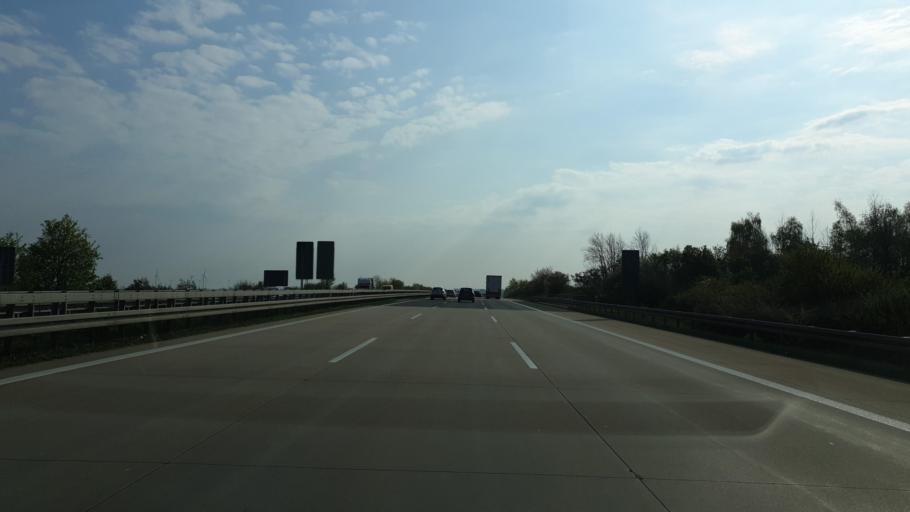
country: DE
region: Saxony
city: Hainichen
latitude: 50.9978
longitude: 13.1493
